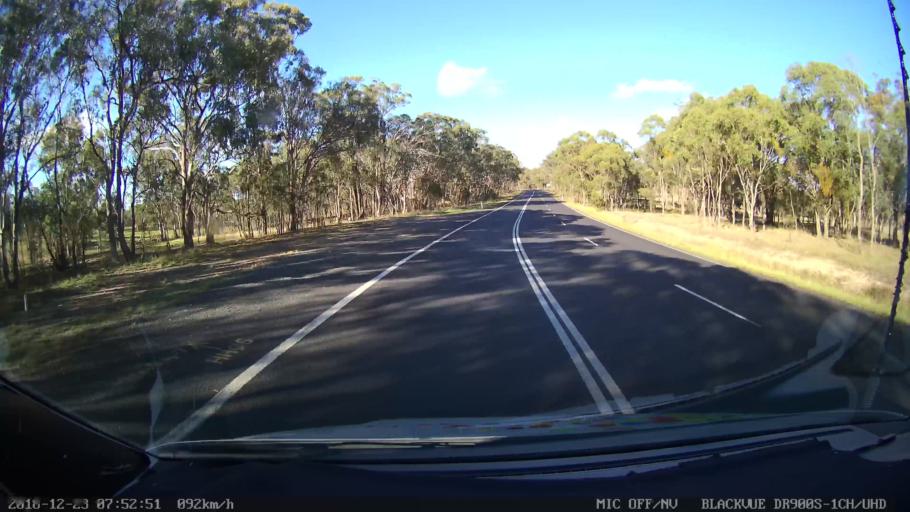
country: AU
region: New South Wales
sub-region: Armidale Dumaresq
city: Armidale
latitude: -30.5324
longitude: 151.8158
